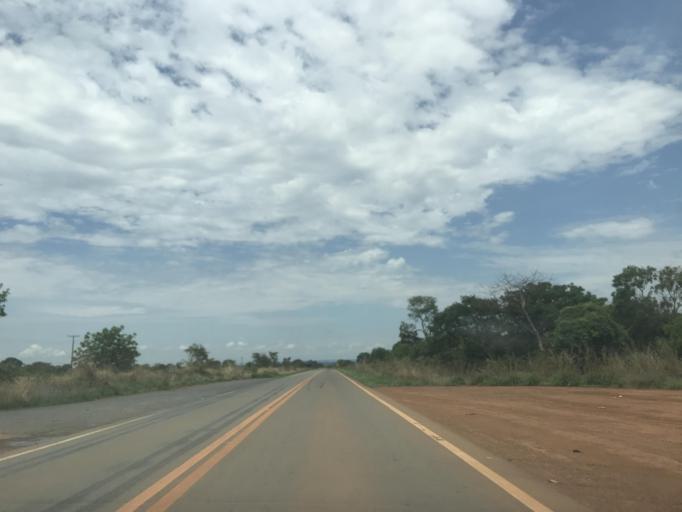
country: BR
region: Goias
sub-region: Luziania
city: Luziania
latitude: -16.3462
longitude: -48.0217
